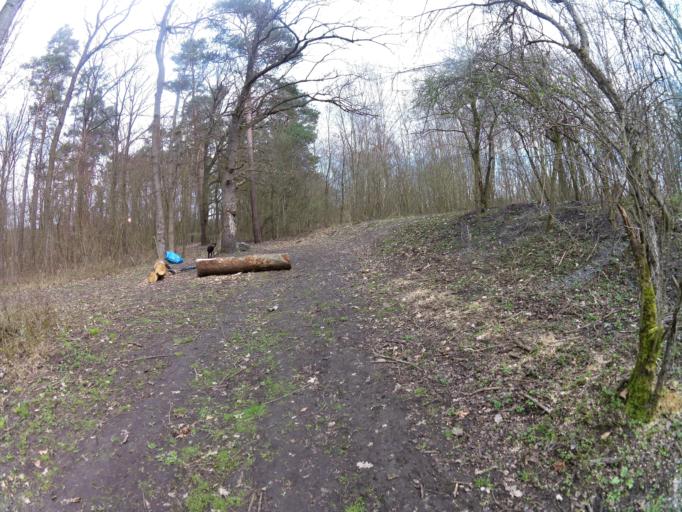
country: PL
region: West Pomeranian Voivodeship
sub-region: Powiat mysliborski
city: Mysliborz
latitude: 52.9380
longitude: 14.8538
